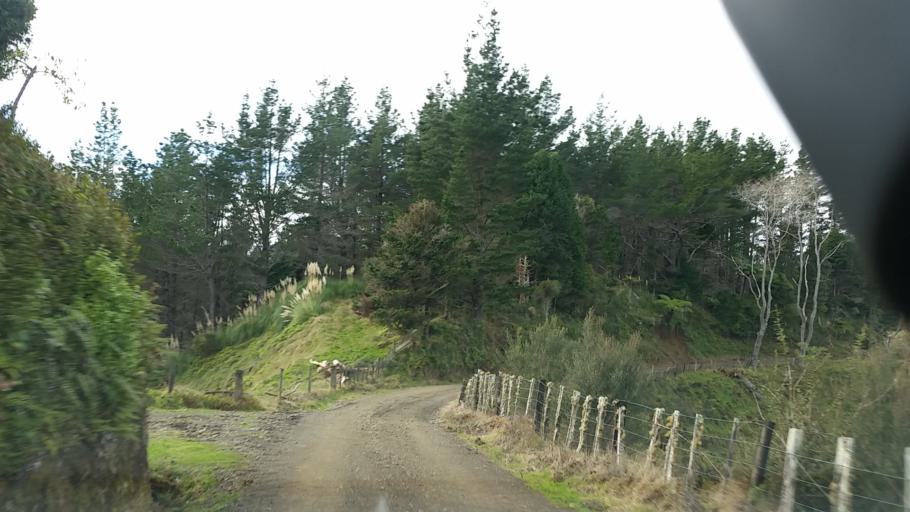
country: NZ
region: Taranaki
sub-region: New Plymouth District
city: Waitara
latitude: -39.0402
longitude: 174.4166
